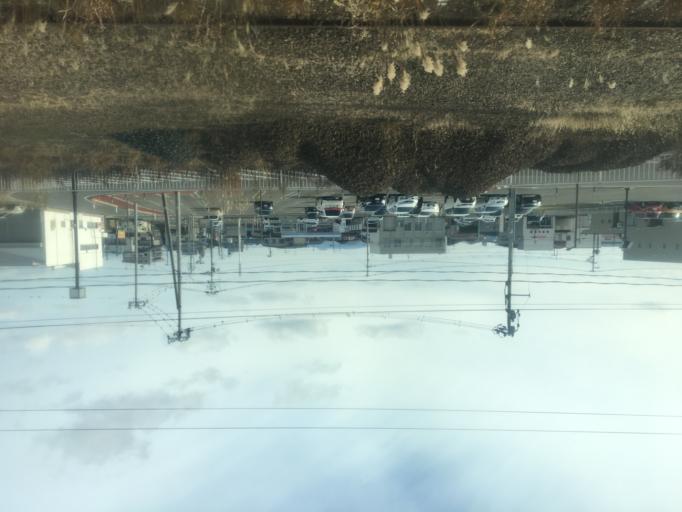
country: JP
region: Akita
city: Tenno
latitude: 39.9488
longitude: 140.0782
